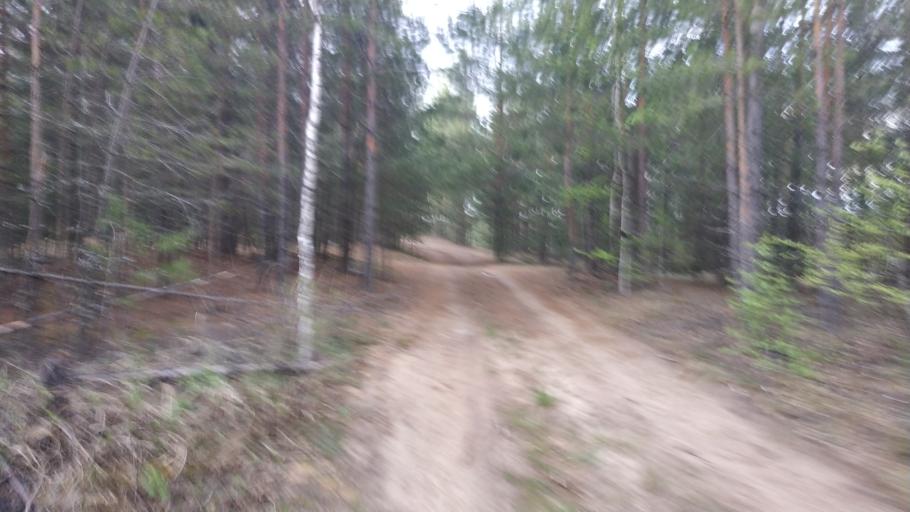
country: RU
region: Chuvashia
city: Novocheboksarsk
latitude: 56.1616
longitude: 47.4630
